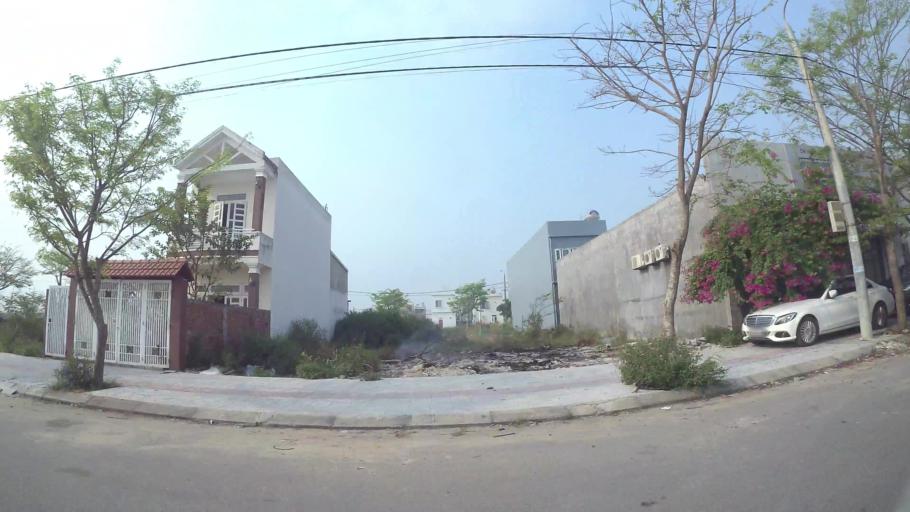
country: VN
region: Da Nang
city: Ngu Hanh Son
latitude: 16.0055
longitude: 108.2283
